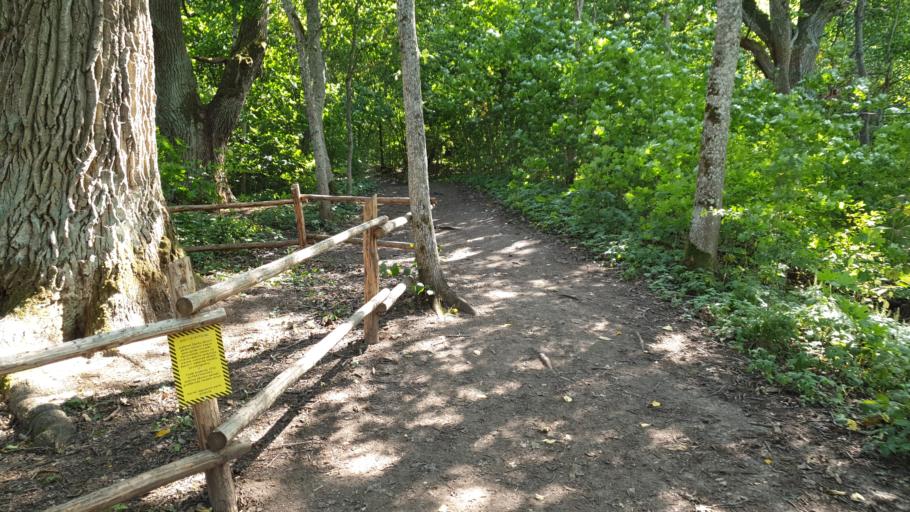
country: LT
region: Vilnius County
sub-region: Vilniaus Rajonas
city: Vievis
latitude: 54.8195
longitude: 24.9367
